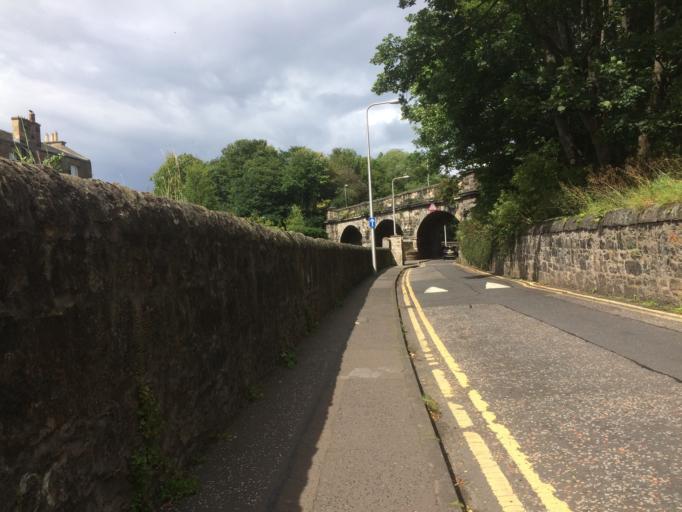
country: GB
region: Scotland
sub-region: Edinburgh
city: Edinburgh
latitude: 55.9648
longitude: -3.1989
